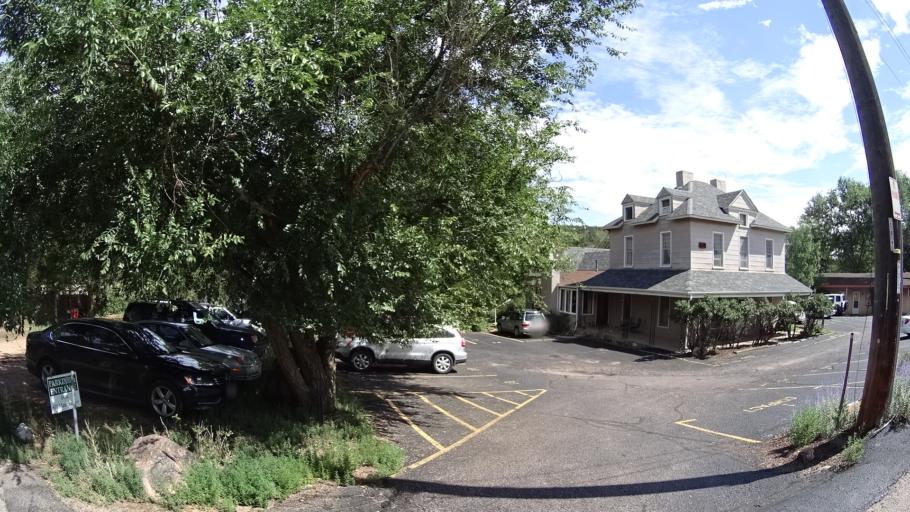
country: US
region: Colorado
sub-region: El Paso County
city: Manitou Springs
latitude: 38.8566
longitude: -104.9137
